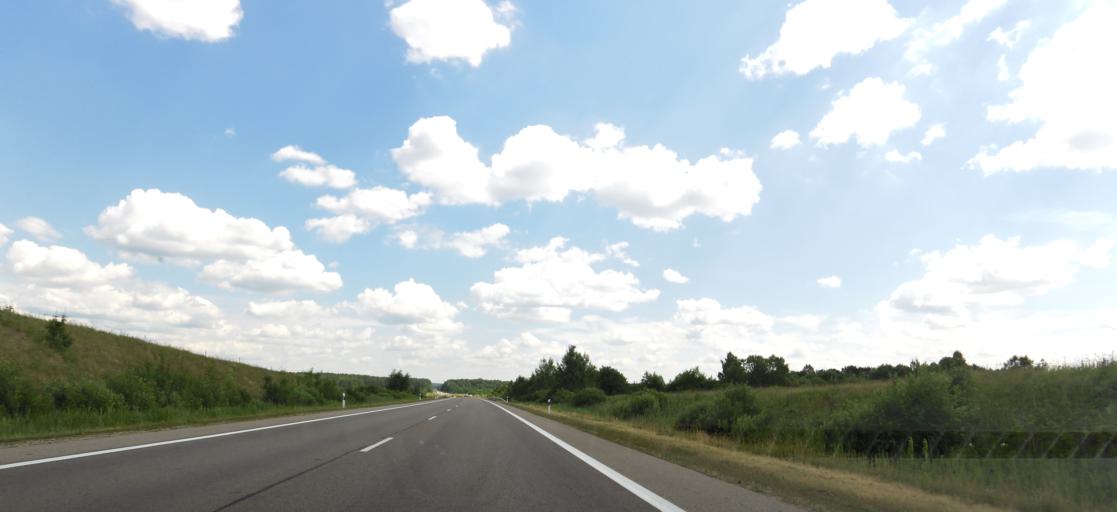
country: LT
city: Skaidiskes
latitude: 54.5985
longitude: 25.5009
